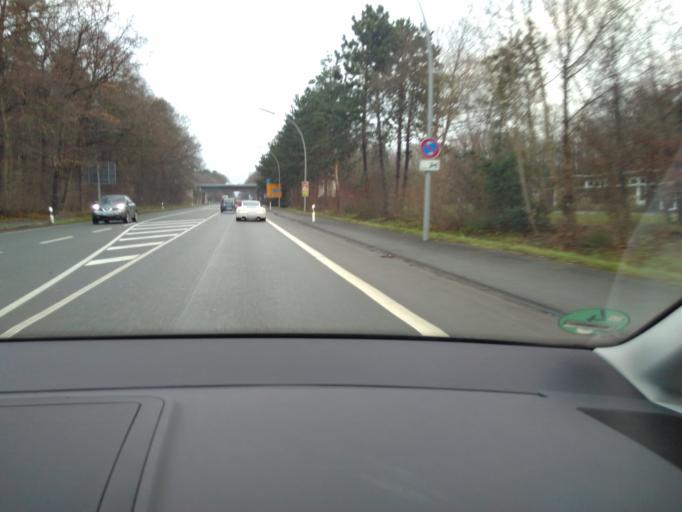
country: DE
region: North Rhine-Westphalia
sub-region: Regierungsbezirk Detmold
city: Rheda-Wiedenbruck
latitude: 51.8503
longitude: 8.3251
